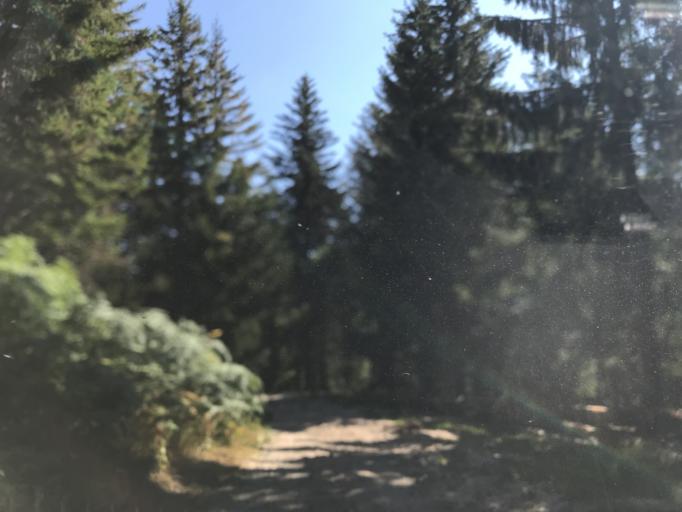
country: FR
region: Rhone-Alpes
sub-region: Departement de la Loire
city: Noiretable
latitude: 45.7603
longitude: 3.7587
